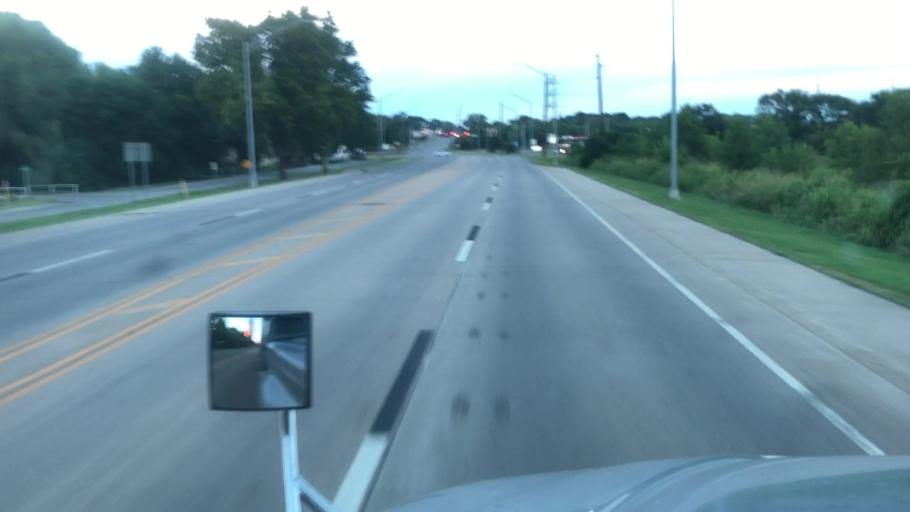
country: US
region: Oklahoma
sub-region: Kay County
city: Ponca City
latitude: 36.6928
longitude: -97.0669
